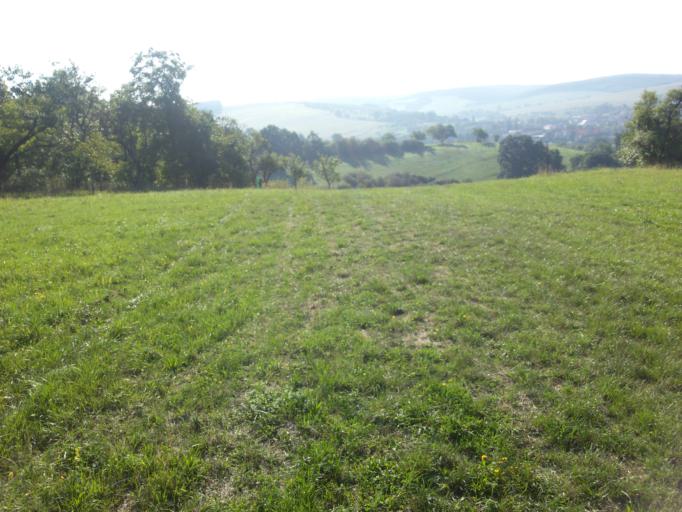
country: CZ
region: Zlin
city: Brezolupy
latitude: 49.1060
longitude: 17.5840
